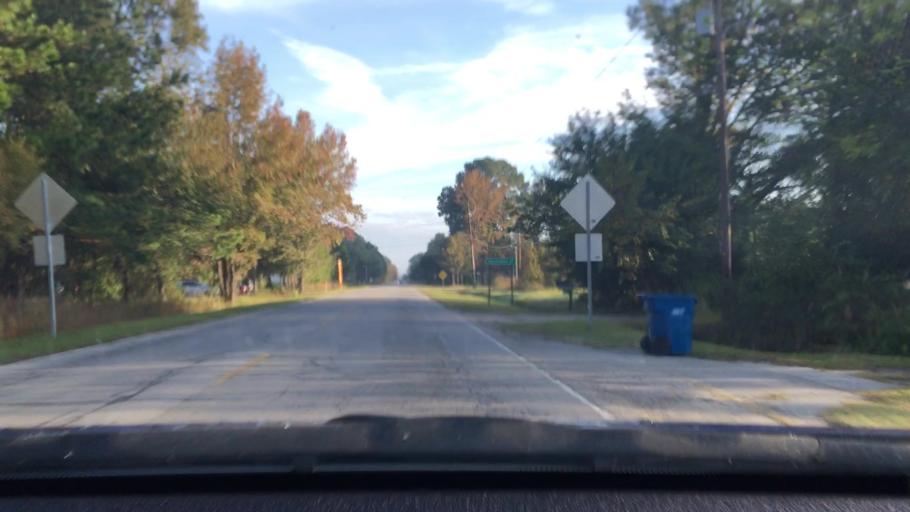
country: US
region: South Carolina
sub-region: Sumter County
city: East Sumter
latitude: 33.9392
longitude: -80.3181
